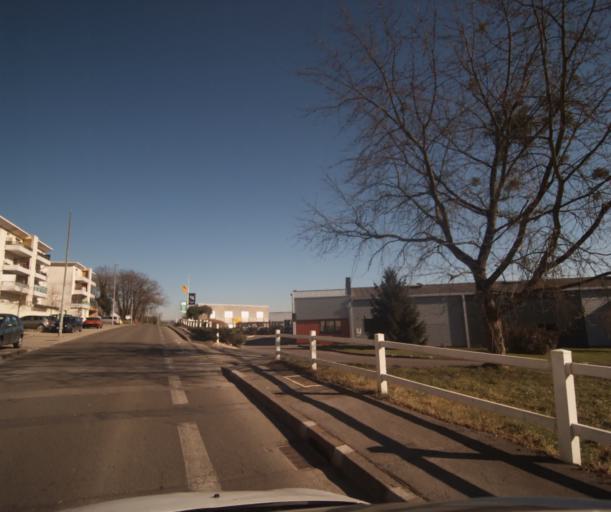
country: FR
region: Franche-Comte
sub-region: Departement du Doubs
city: Pirey
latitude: 47.2355
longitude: 5.9769
